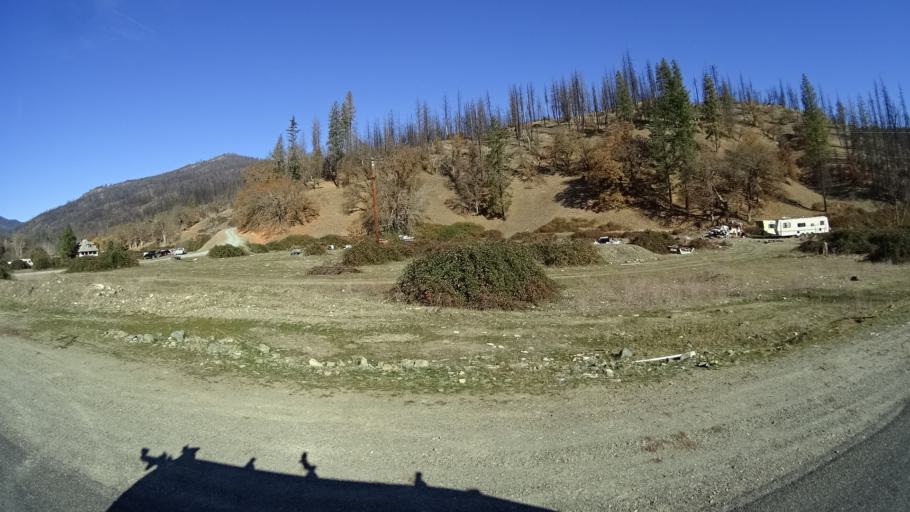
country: US
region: California
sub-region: Siskiyou County
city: Happy Camp
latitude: 41.8420
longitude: -123.0319
